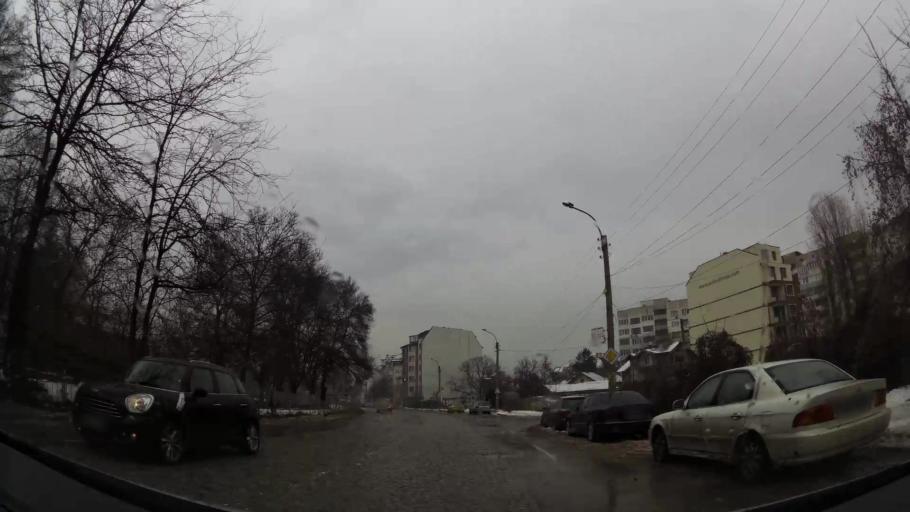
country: BG
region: Sofia-Capital
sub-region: Stolichna Obshtina
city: Sofia
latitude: 42.6719
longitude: 23.2612
